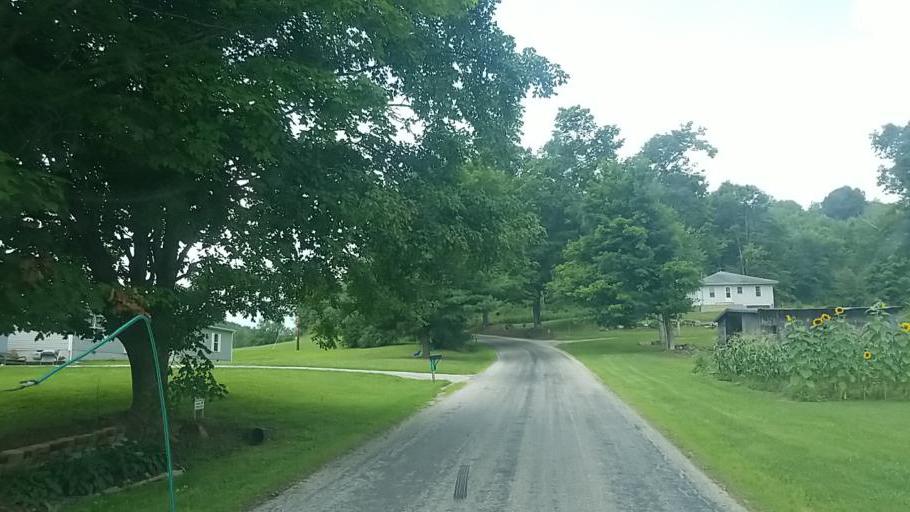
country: US
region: Ohio
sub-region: Muskingum County
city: Frazeysburg
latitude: 40.2225
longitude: -82.2149
